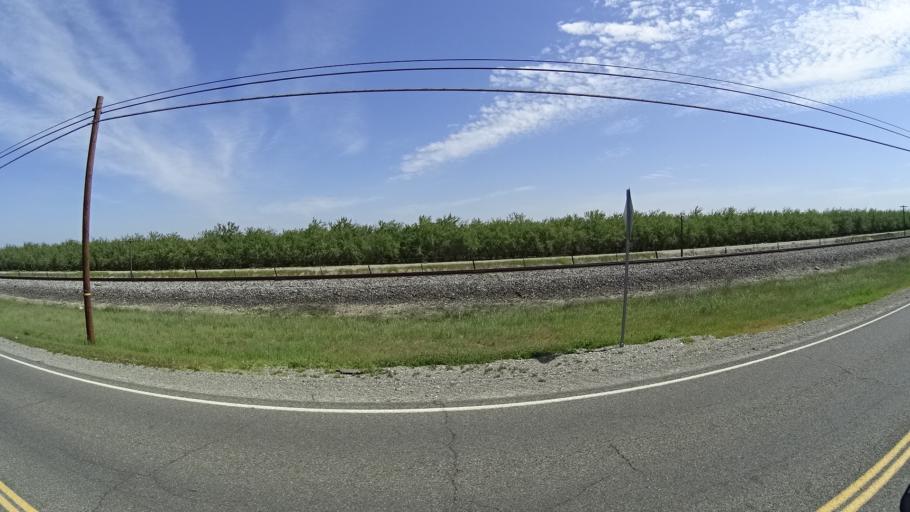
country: US
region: California
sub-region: Glenn County
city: Willows
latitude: 39.5715
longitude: -122.1939
